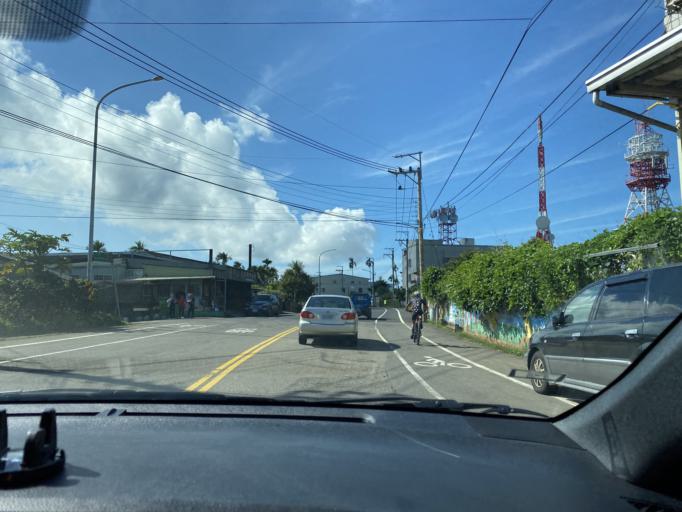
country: TW
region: Taiwan
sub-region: Nantou
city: Nantou
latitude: 23.9429
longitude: 120.6366
